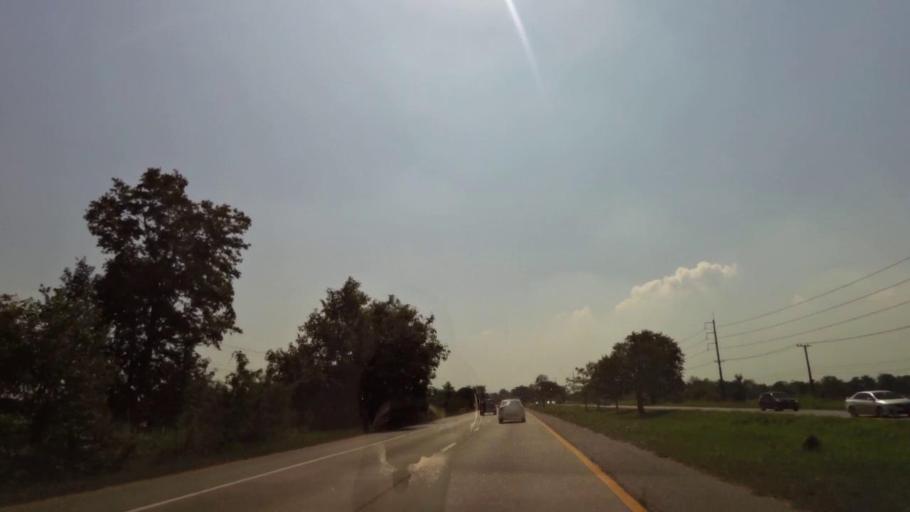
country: TH
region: Phichit
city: Wachira Barami
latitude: 16.5919
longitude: 100.1469
